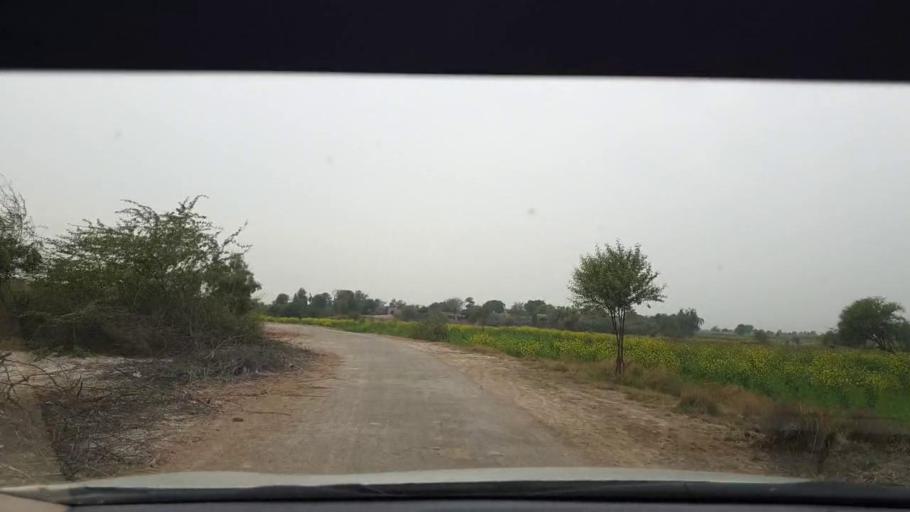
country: PK
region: Sindh
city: Berani
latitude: 25.8744
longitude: 68.7984
